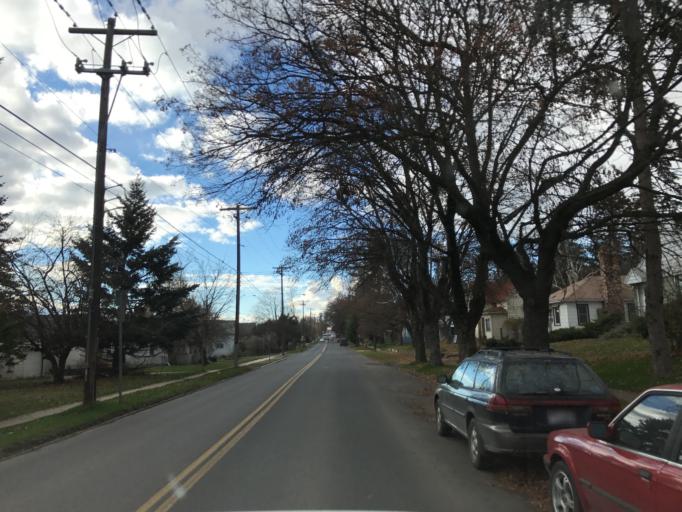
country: US
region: Idaho
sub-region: Latah County
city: Moscow
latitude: 46.7346
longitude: -117.0068
